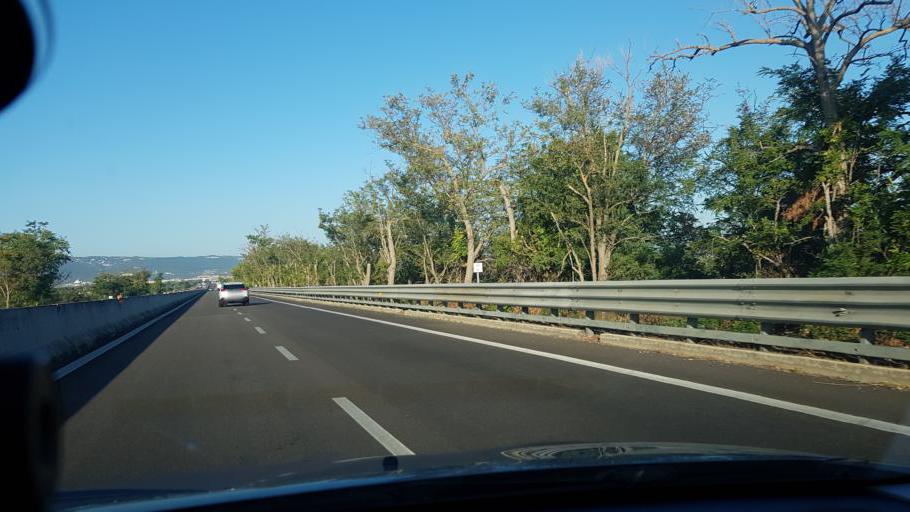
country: IT
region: Apulia
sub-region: Provincia di Brindisi
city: Pezze di Greco
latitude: 40.8336
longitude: 17.4196
